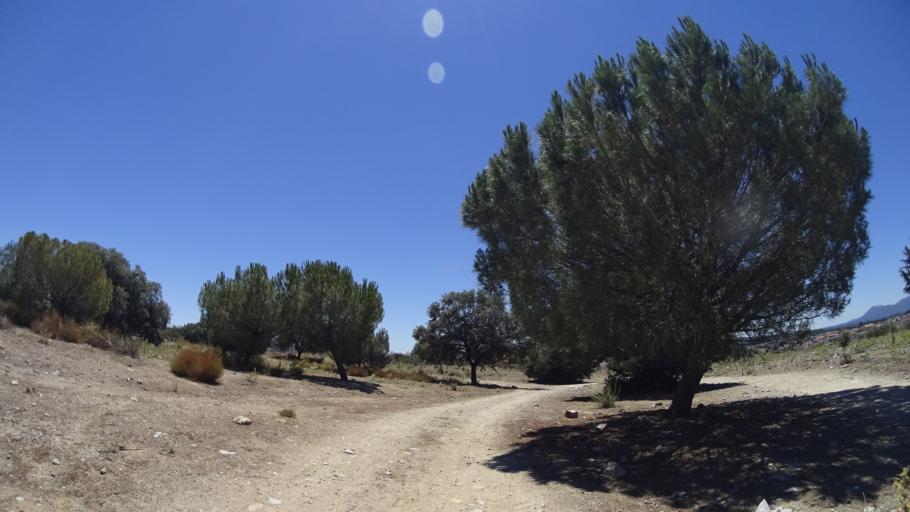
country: ES
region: Madrid
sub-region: Provincia de Madrid
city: Alpedrete
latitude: 40.6652
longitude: -4.0188
